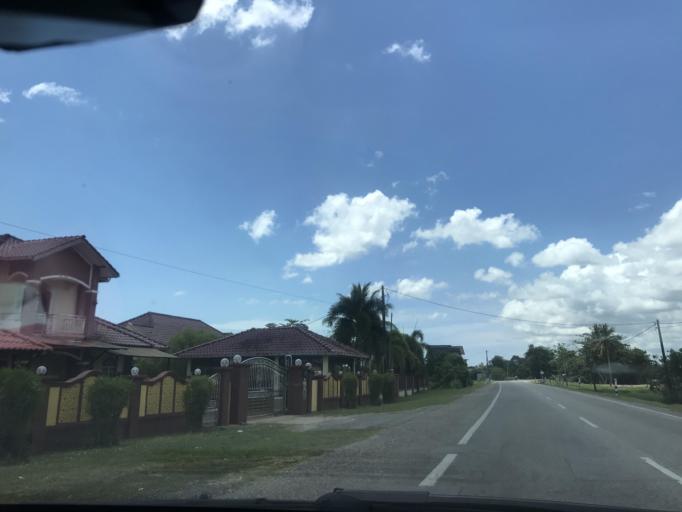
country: MY
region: Kelantan
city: Tumpat
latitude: 6.2083
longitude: 102.1121
